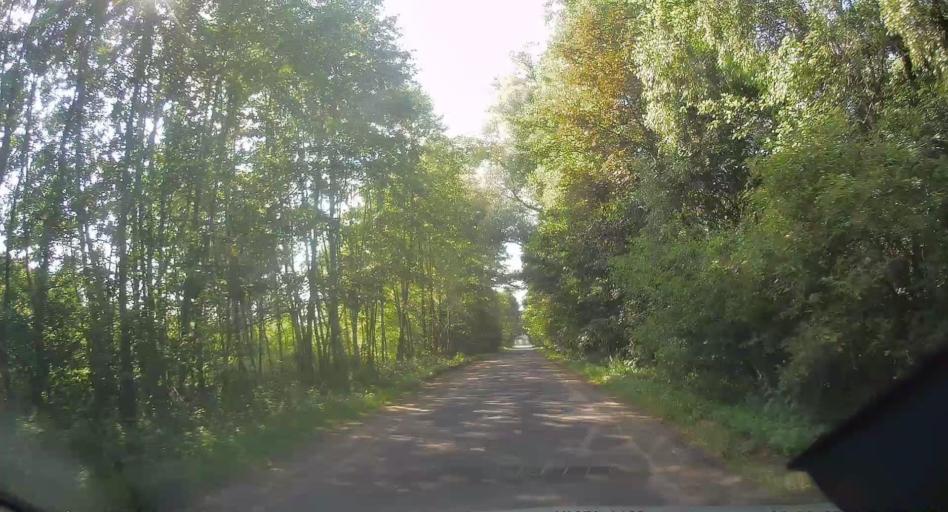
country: PL
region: Swietokrzyskie
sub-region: Powiat konecki
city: Ruda Maleniecka
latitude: 51.1304
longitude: 20.2468
